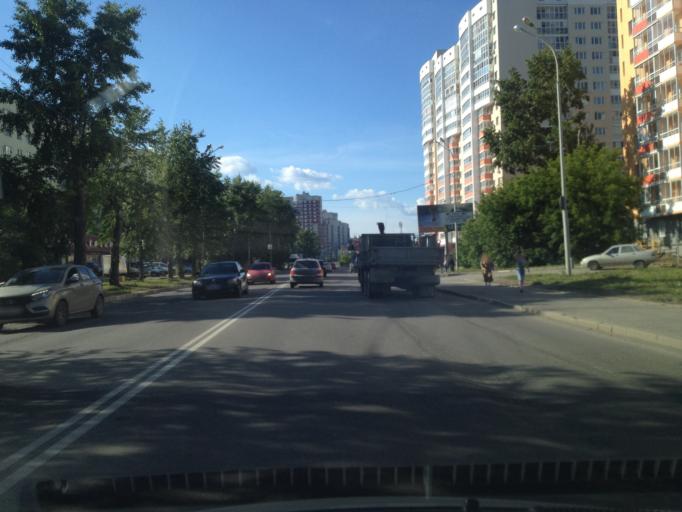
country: RU
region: Sverdlovsk
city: Yekaterinburg
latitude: 56.9054
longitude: 60.6219
